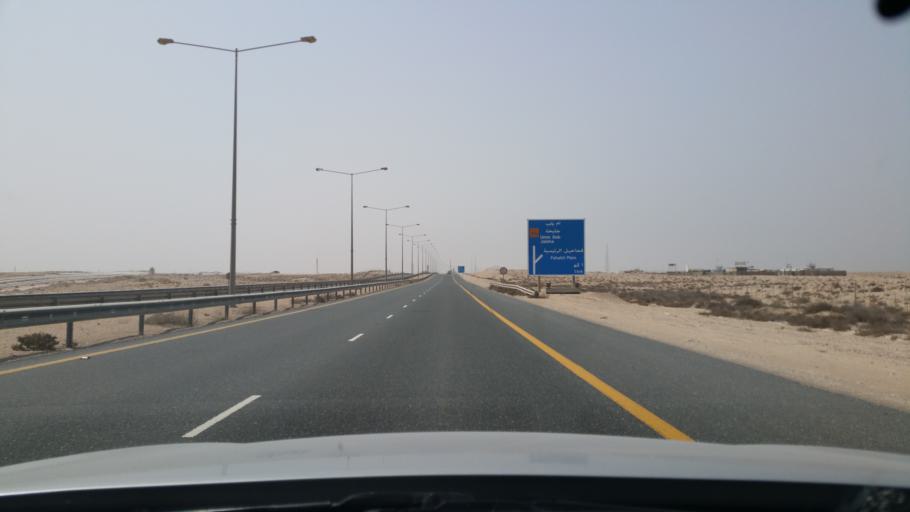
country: QA
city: Umm Bab
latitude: 25.3075
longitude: 50.7921
